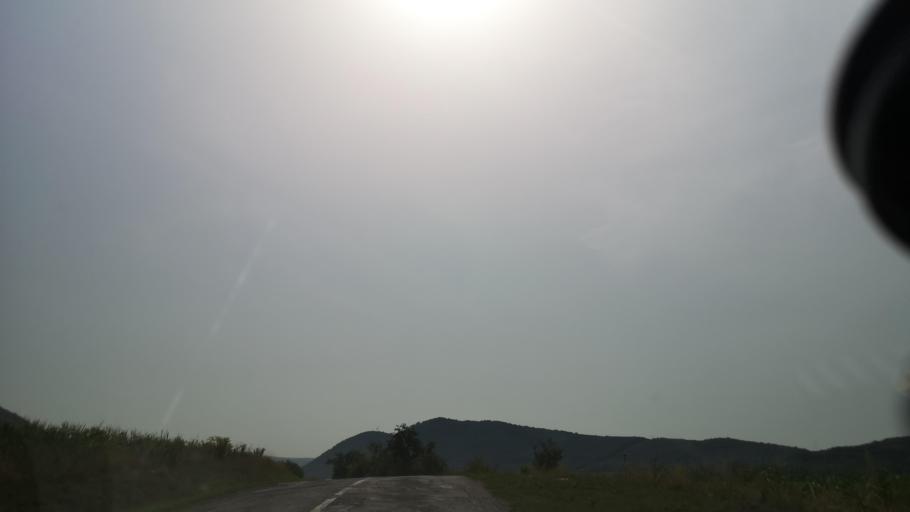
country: SK
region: Banskobystricky
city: Revuca
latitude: 48.6106
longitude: 20.2301
